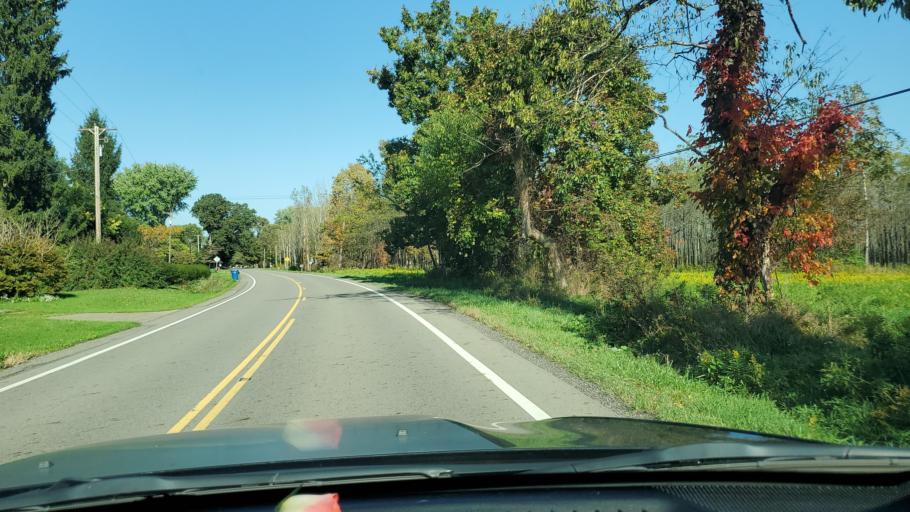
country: US
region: Ohio
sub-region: Trumbull County
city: Cortland
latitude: 41.4199
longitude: -80.5809
